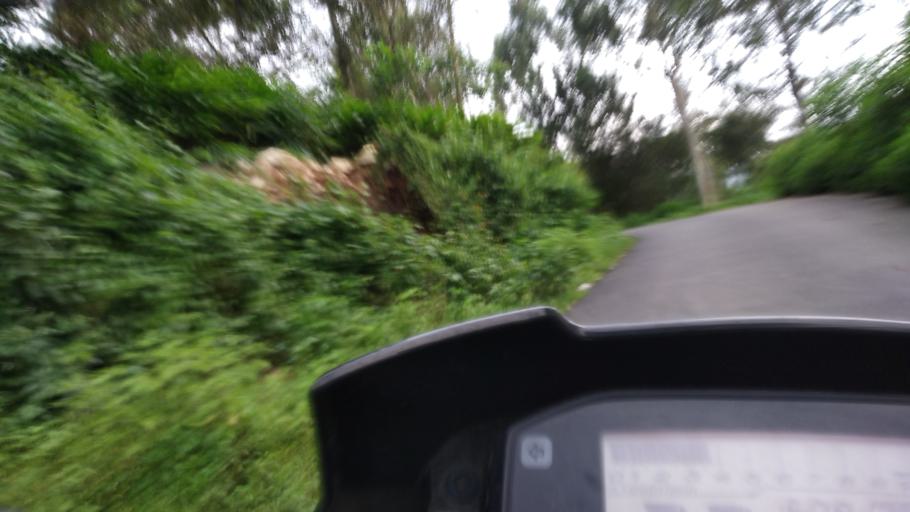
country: IN
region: Tamil Nadu
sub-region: Theni
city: Bodinayakkanur
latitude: 10.0288
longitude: 77.2306
